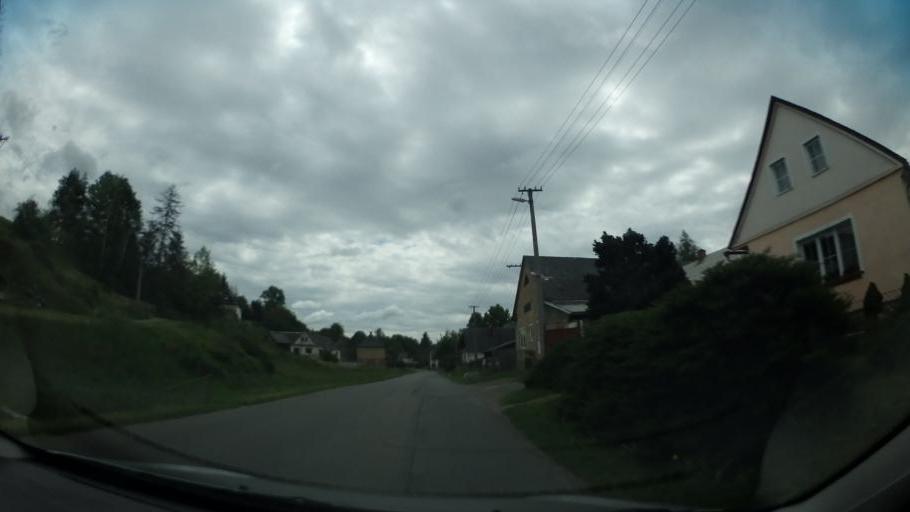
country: CZ
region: Pardubicky
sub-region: Okres Svitavy
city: Moravska Trebova
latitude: 49.8284
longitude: 16.7023
